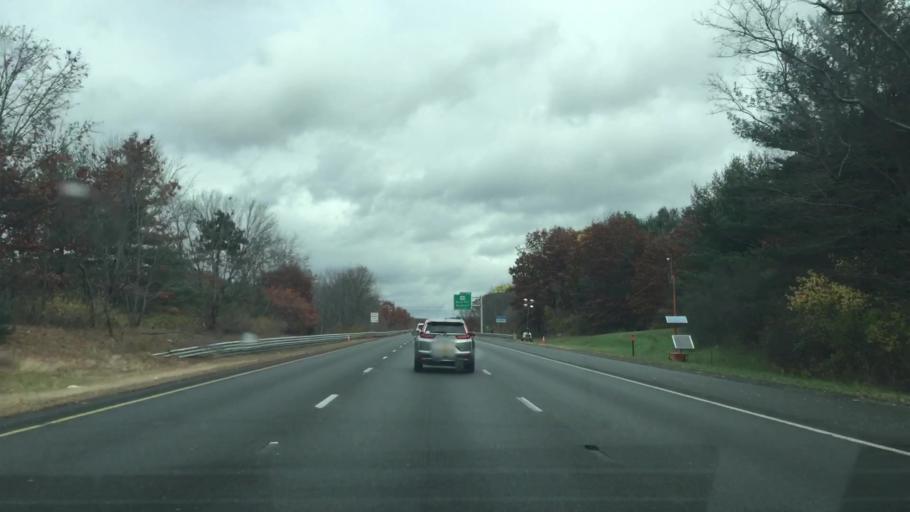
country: US
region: Massachusetts
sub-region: Essex County
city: North Andover
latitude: 42.7484
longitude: -71.1347
